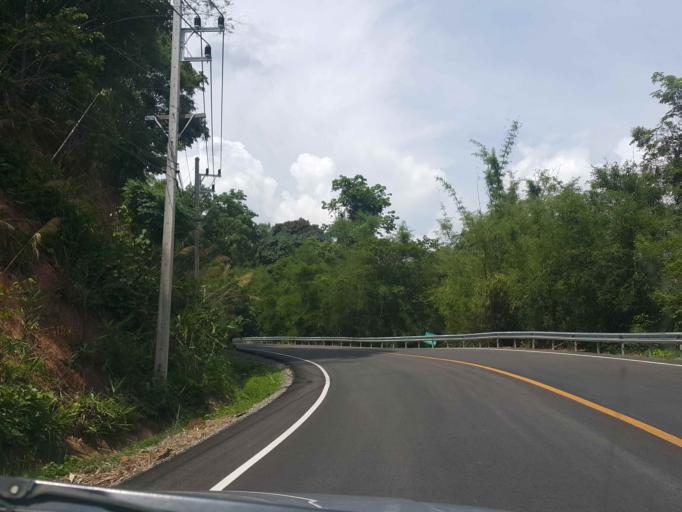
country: TH
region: Nan
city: Ban Luang
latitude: 18.8738
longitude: 100.5091
